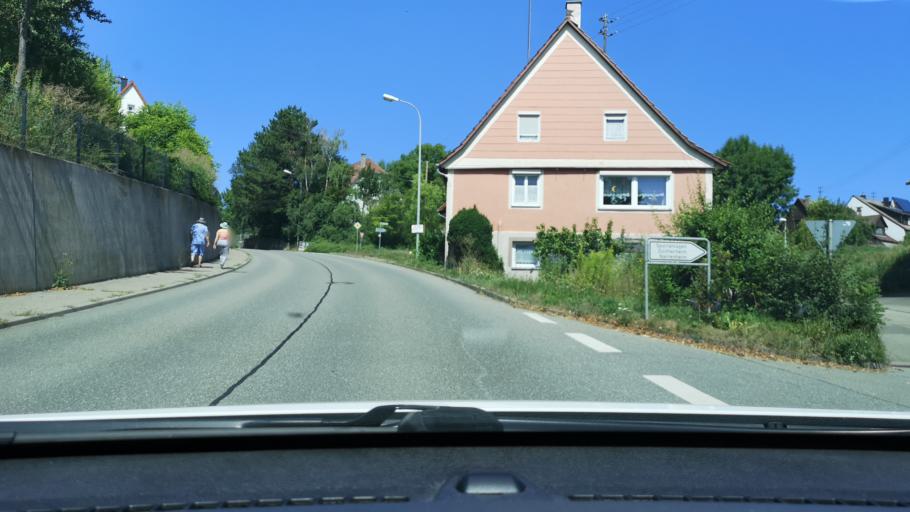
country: DE
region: Baden-Wuerttemberg
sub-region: Freiburg Region
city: Vohringen
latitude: 48.3476
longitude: 8.6848
